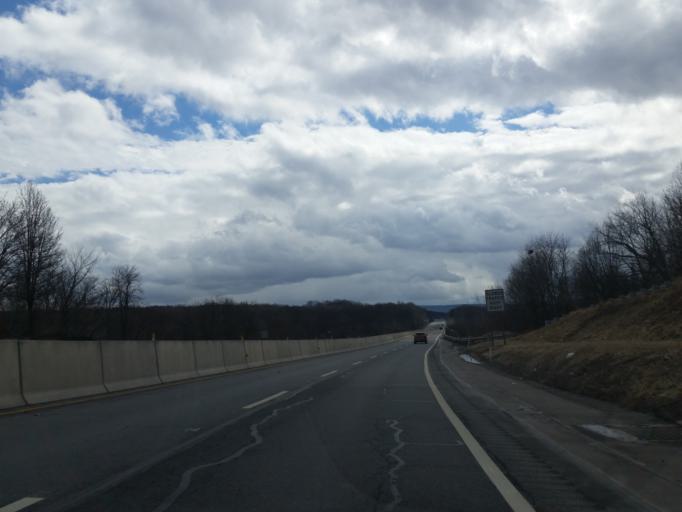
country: US
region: Pennsylvania
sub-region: Lackawanna County
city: Old Forge
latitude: 41.3775
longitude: -75.7207
